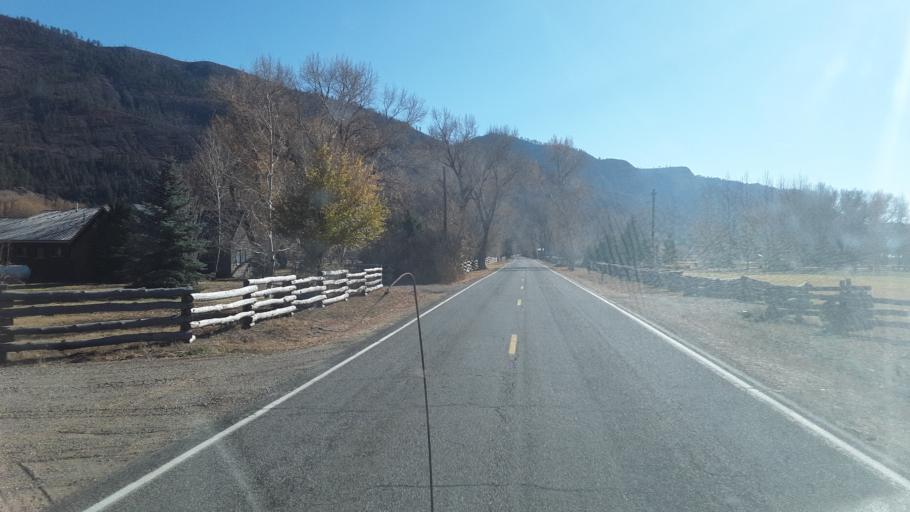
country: US
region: Colorado
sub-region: La Plata County
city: Durango
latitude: 37.4334
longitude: -107.7996
